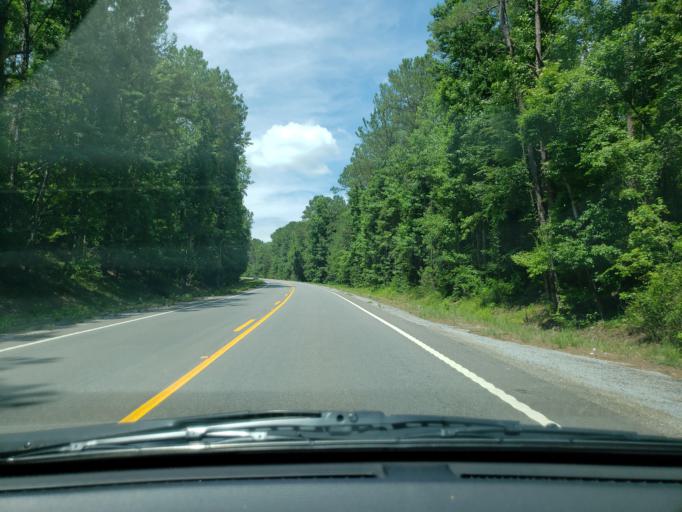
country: US
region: Alabama
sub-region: Elmore County
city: Eclectic
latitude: 32.6524
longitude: -85.9455
